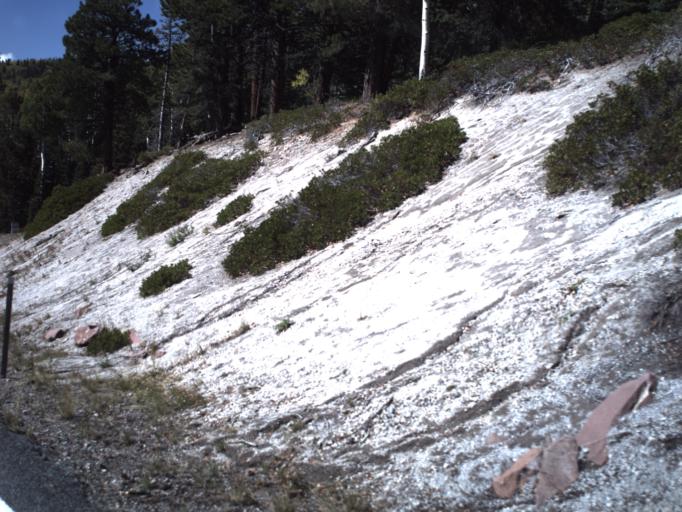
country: US
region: Utah
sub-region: Piute County
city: Junction
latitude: 38.3125
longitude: -112.3968
